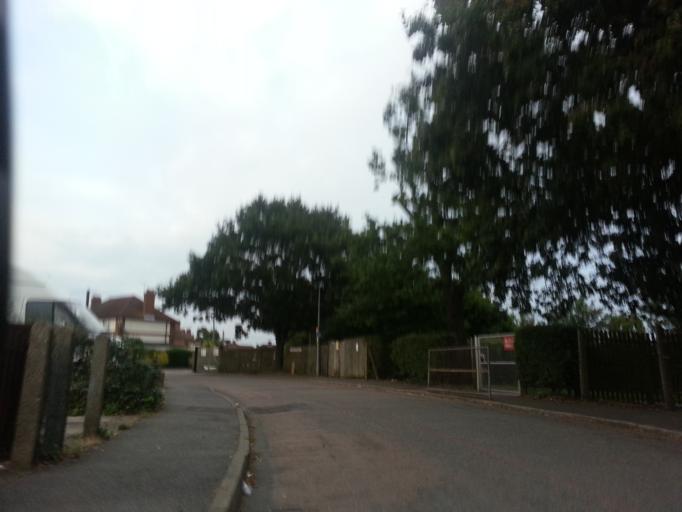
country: GB
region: England
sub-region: Suffolk
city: Ipswich
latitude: 52.0297
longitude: 1.1783
